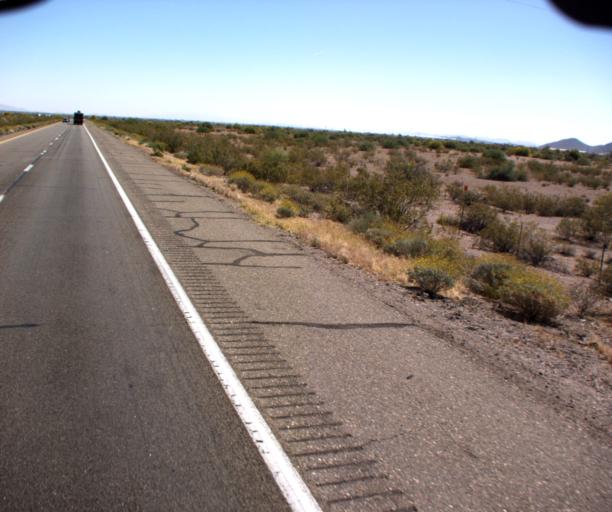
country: US
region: Arizona
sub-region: Maricopa County
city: Buckeye
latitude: 33.5037
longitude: -112.9717
